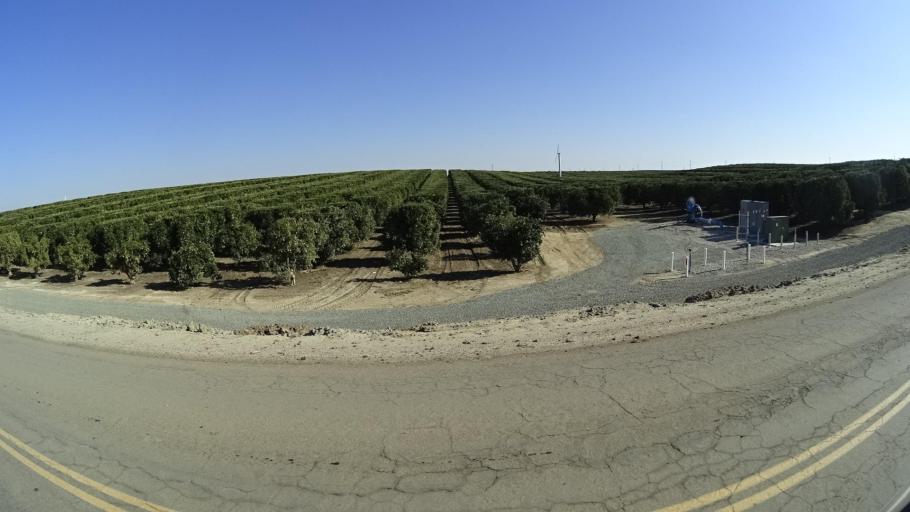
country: US
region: California
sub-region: Tulare County
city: Richgrove
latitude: 35.7066
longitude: -119.1338
